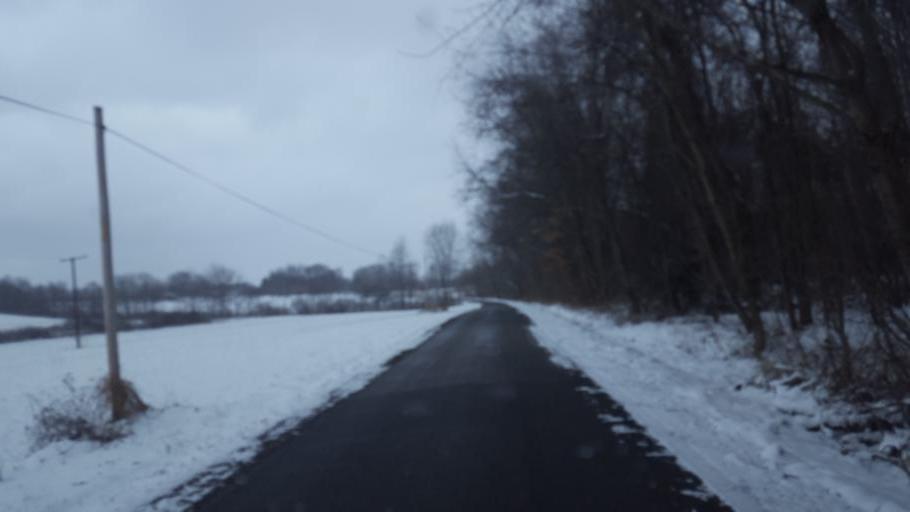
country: US
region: Pennsylvania
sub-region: Mercer County
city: Stoneboro
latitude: 41.3996
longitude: -80.0856
